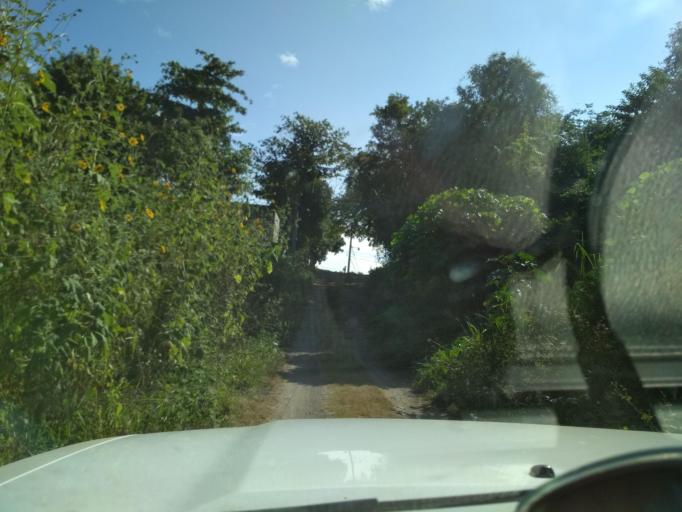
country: MX
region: Veracruz
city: Rinconada
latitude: 19.3566
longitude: -96.5620
